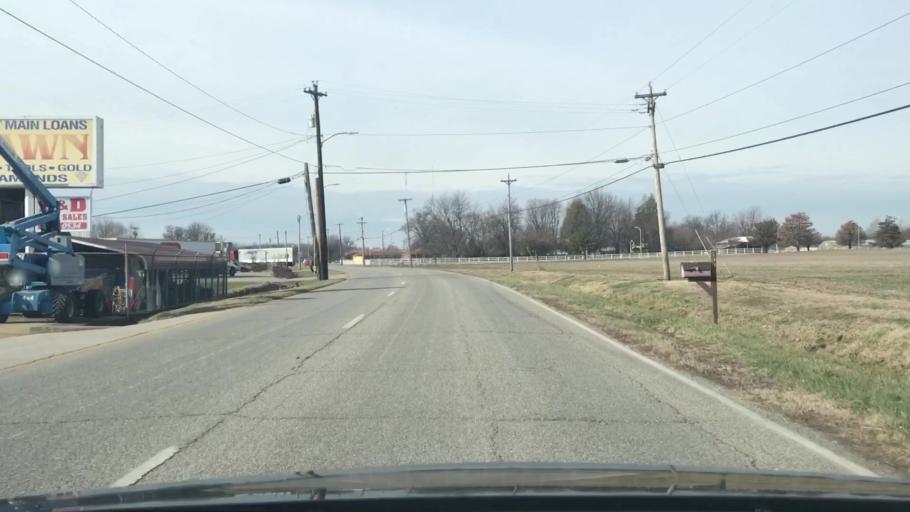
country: US
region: Kentucky
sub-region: Daviess County
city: Owensboro
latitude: 37.7740
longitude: -87.1460
